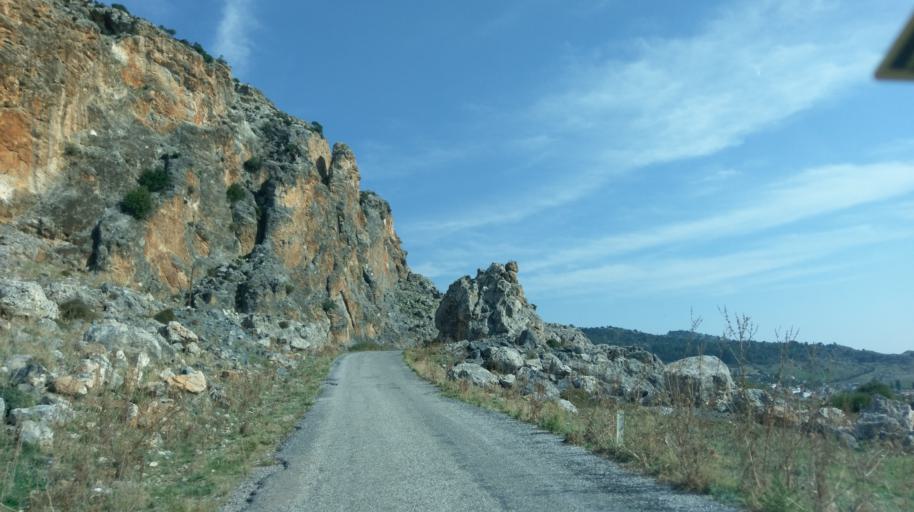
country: CY
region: Keryneia
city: Lapithos
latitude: 35.3146
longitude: 33.1304
